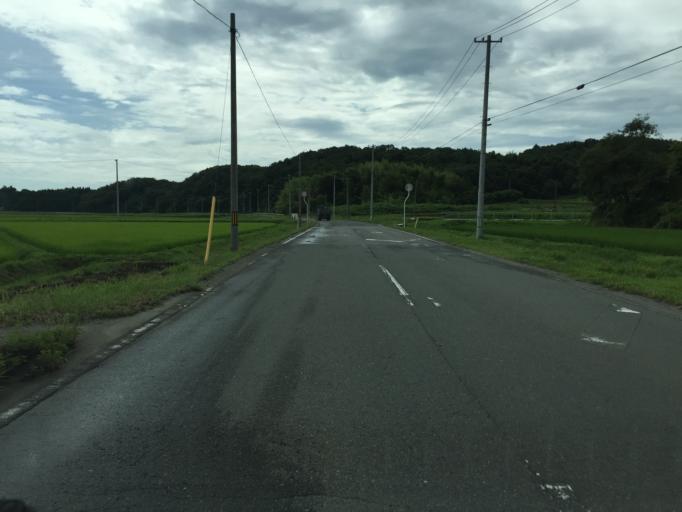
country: JP
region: Miyagi
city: Marumori
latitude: 37.7682
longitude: 140.9617
